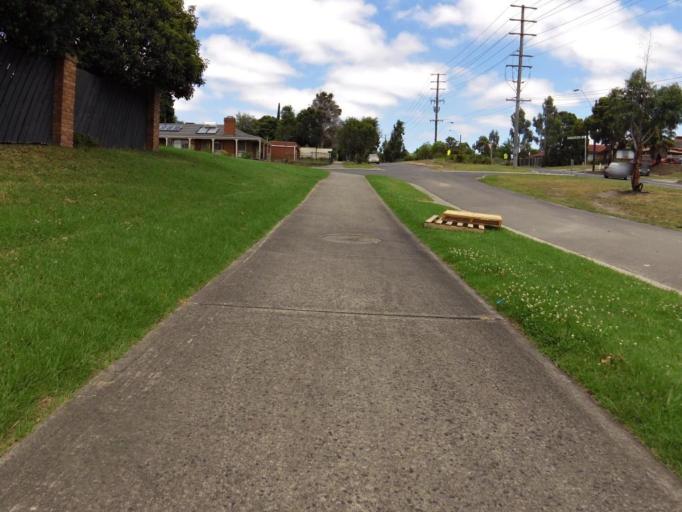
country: AU
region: Victoria
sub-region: Casey
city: Endeavour Hills
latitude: -37.9666
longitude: 145.2437
